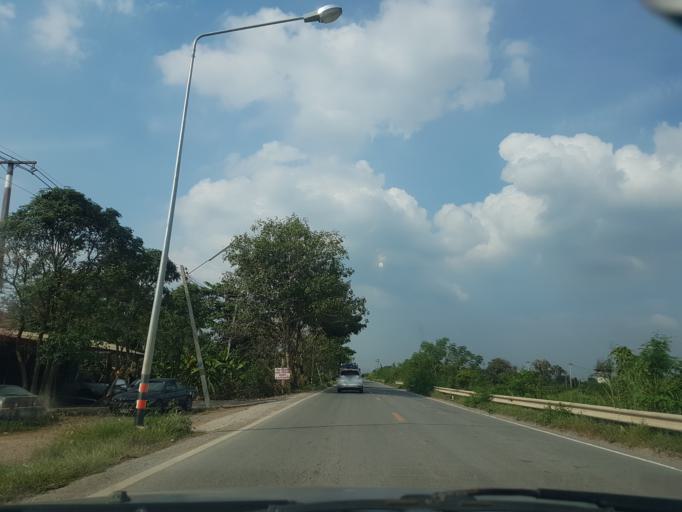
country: TH
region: Phra Nakhon Si Ayutthaya
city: Phachi
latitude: 14.4134
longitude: 100.7834
